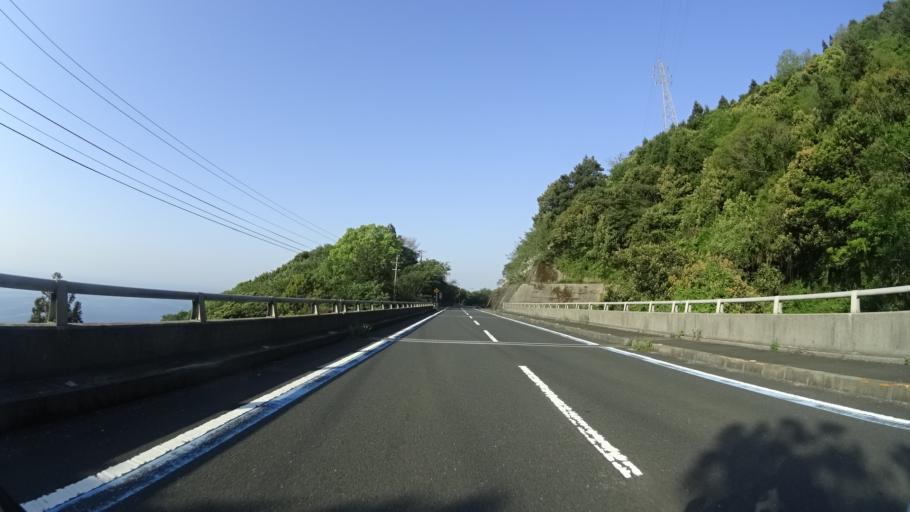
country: JP
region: Ehime
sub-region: Nishiuwa-gun
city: Ikata-cho
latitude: 33.4507
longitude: 132.2712
